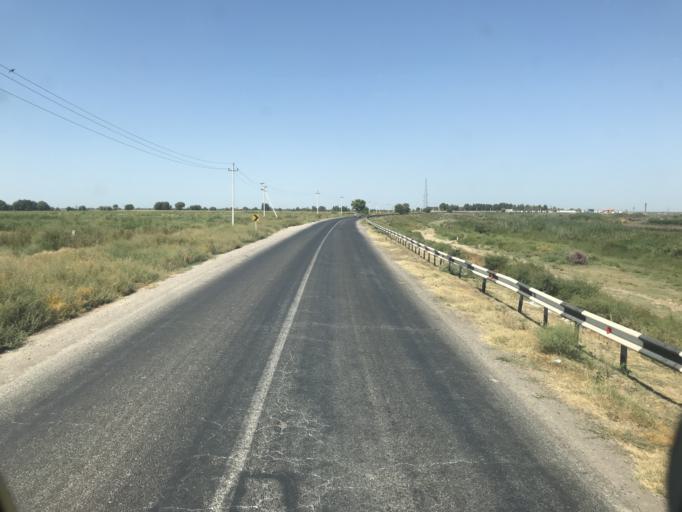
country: KZ
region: Ongtustik Qazaqstan
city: Ilyich
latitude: 40.9505
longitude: 68.4761
